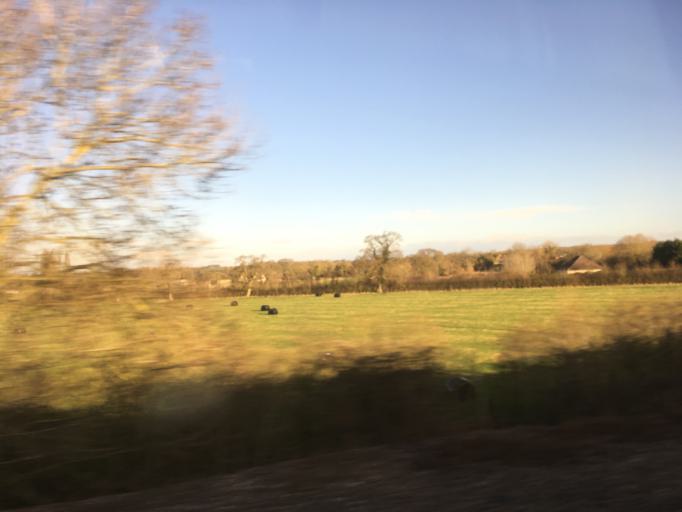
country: GB
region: England
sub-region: Borough of Swindon
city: Wanborough
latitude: 51.5829
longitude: -1.7125
